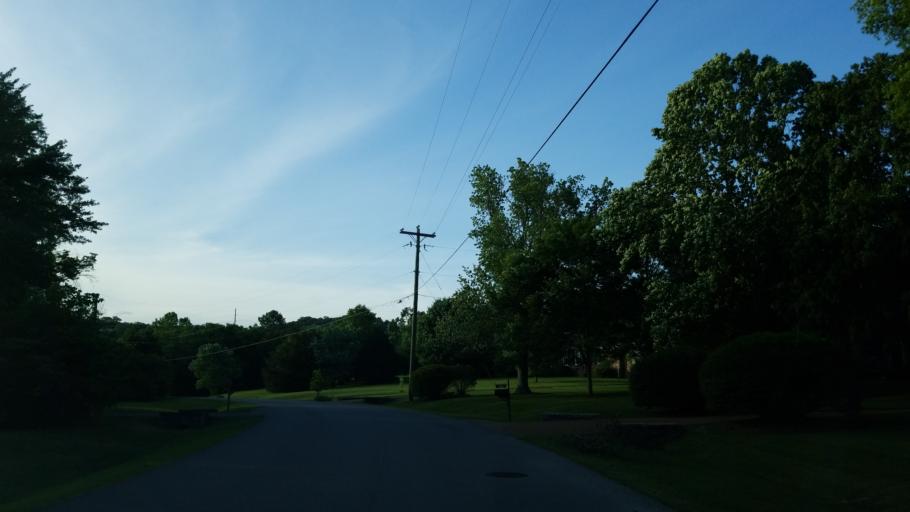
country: US
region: Tennessee
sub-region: Davidson County
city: Forest Hills
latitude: 36.0408
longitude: -86.8415
